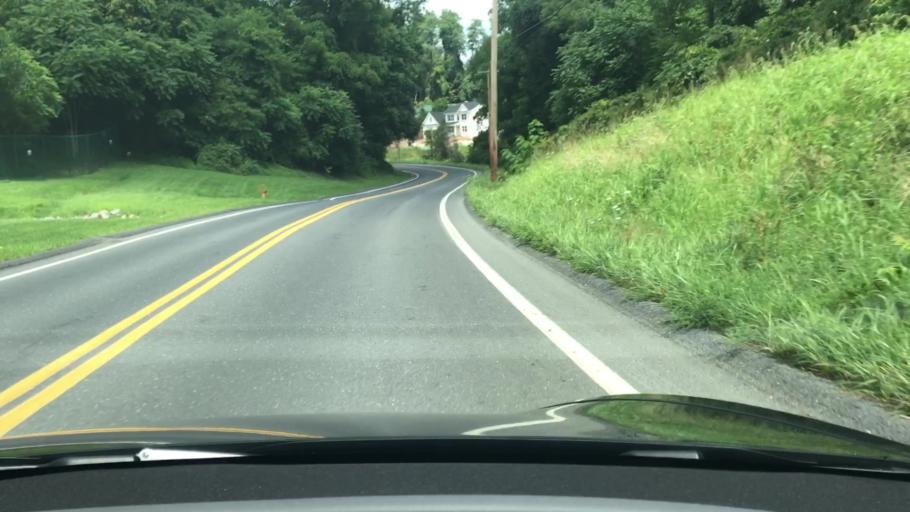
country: US
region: Pennsylvania
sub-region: Cumberland County
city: New Cumberland
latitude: 40.1998
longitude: -76.8785
